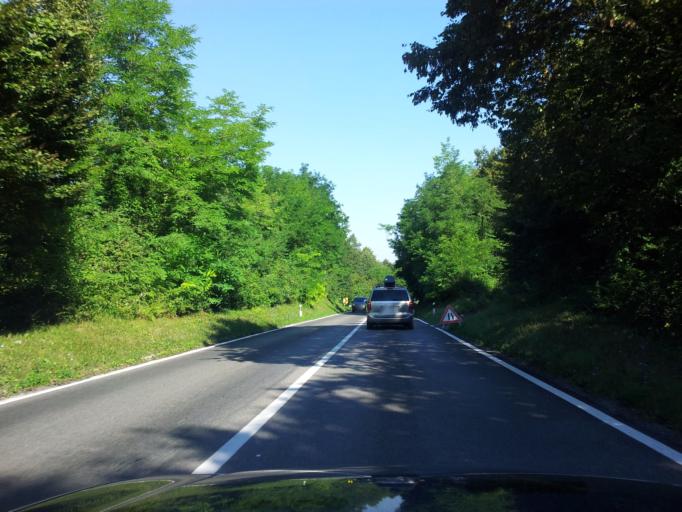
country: HR
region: Karlovacka
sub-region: Grad Karlovac
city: Slunj
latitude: 45.2592
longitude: 15.5524
